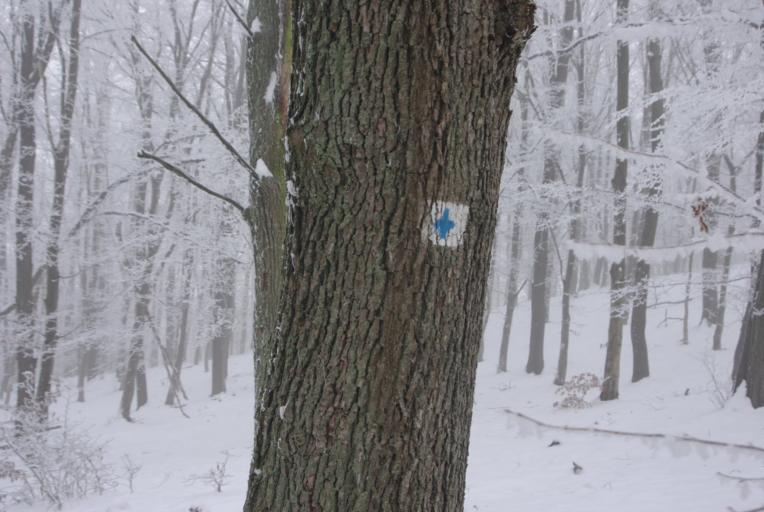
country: HU
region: Pest
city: Pilisszentkereszt
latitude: 47.7011
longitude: 18.9158
